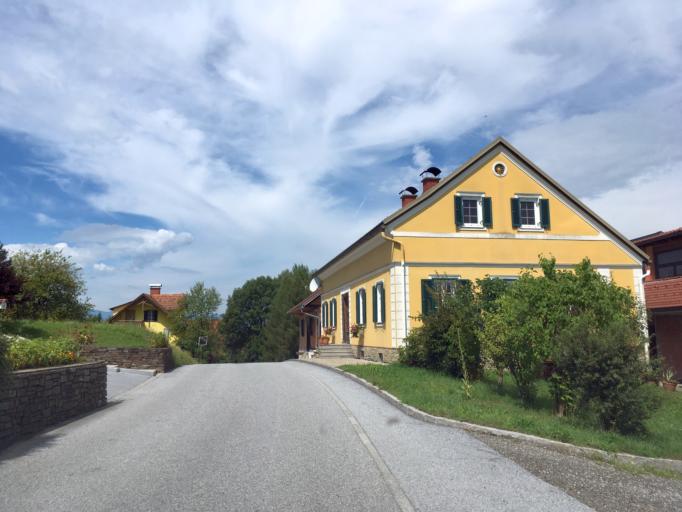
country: AT
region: Styria
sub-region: Politischer Bezirk Leibnitz
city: Pistorf
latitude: 46.7900
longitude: 15.3802
